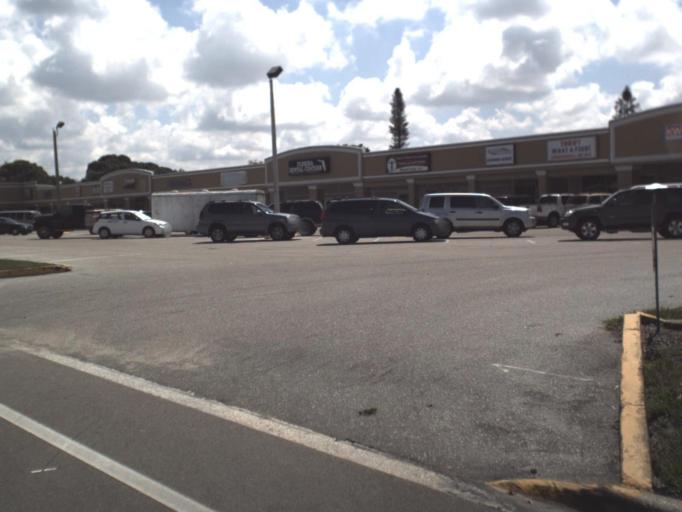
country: US
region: Florida
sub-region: Manatee County
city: West Bradenton
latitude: 27.4958
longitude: -82.6142
